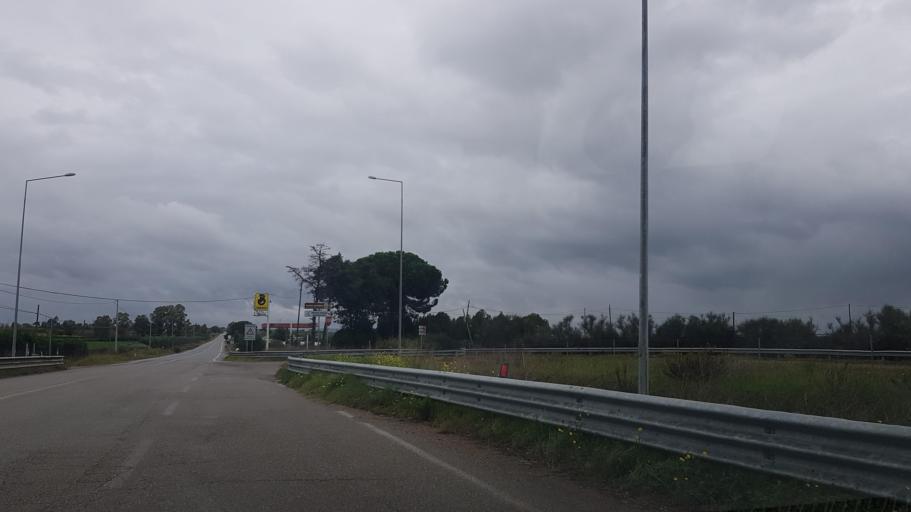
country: IT
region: Apulia
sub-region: Provincia di Taranto
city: Marina di Ginosa
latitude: 40.4043
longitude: 16.8056
